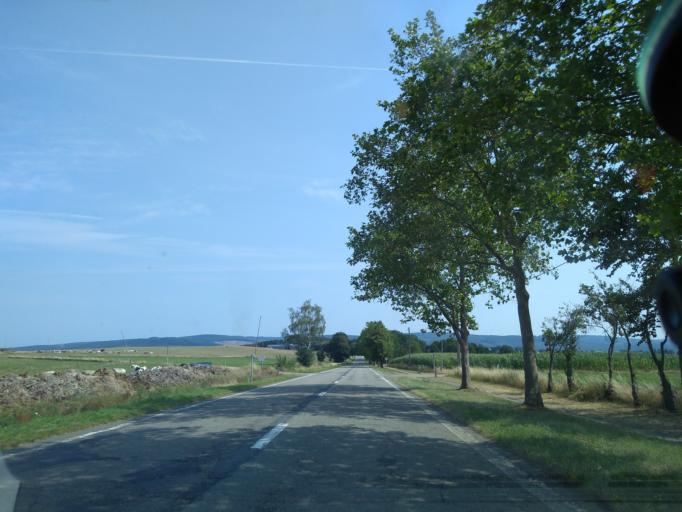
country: BE
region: Wallonia
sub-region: Province du Luxembourg
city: La Roche-en-Ardenne
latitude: 50.1628
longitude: 5.5373
